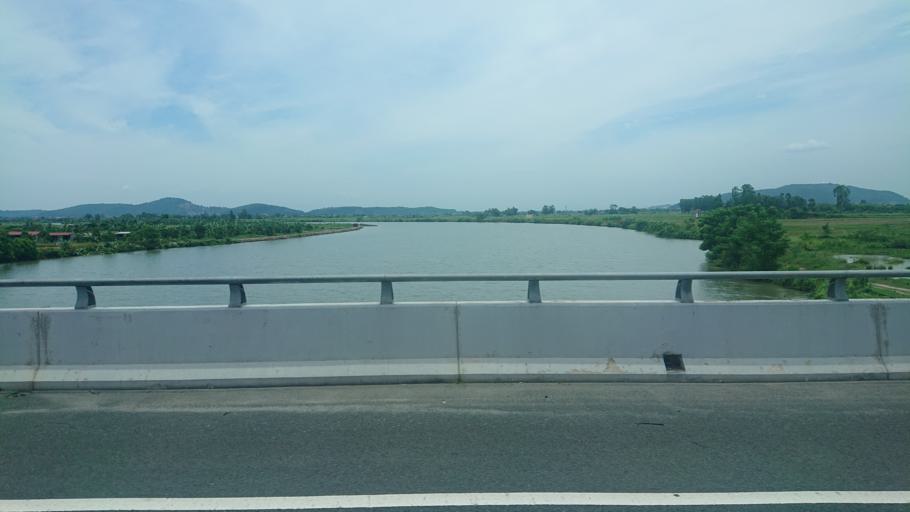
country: VN
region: Hai Phong
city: An Lao
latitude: 20.7765
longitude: 106.5763
